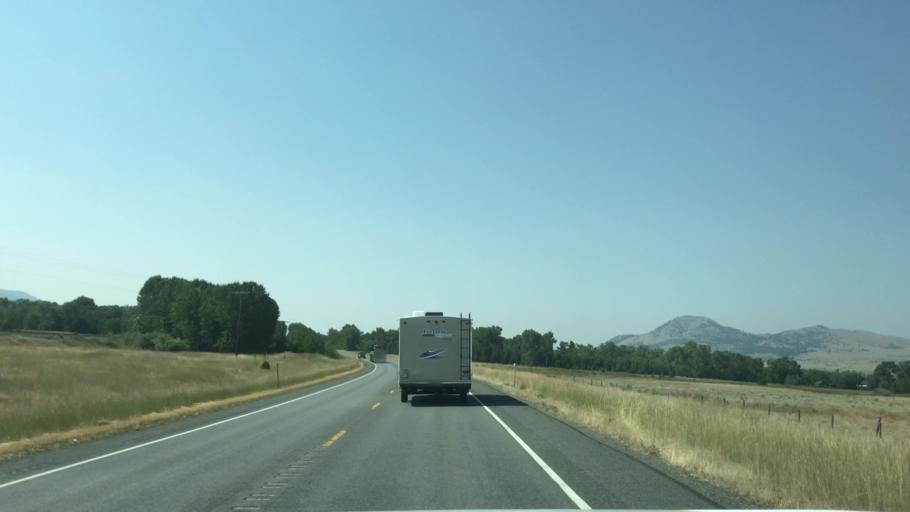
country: US
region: Montana
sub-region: Broadwater County
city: Townsend
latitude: 46.4831
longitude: -111.6645
